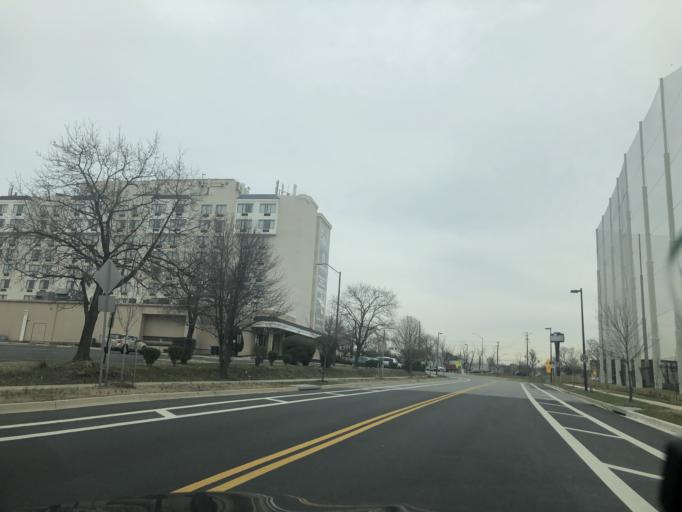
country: US
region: Maryland
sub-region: Prince George's County
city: Oxon Hill
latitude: 38.8009
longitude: -76.9955
